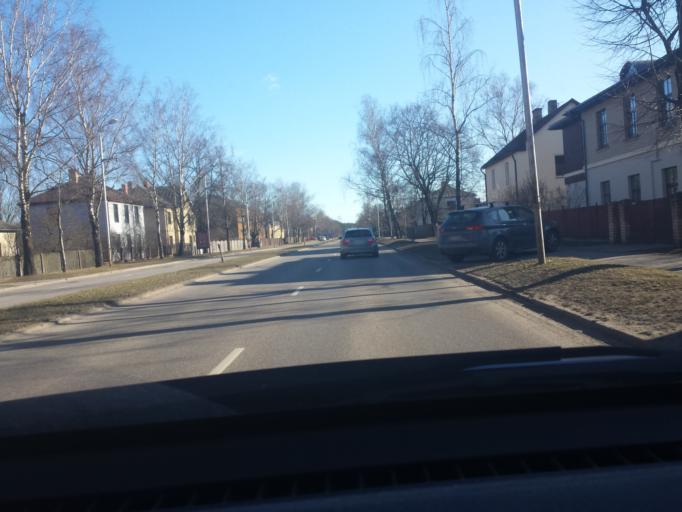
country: LV
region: Riga
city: Jaunciems
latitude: 56.9750
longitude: 24.1891
